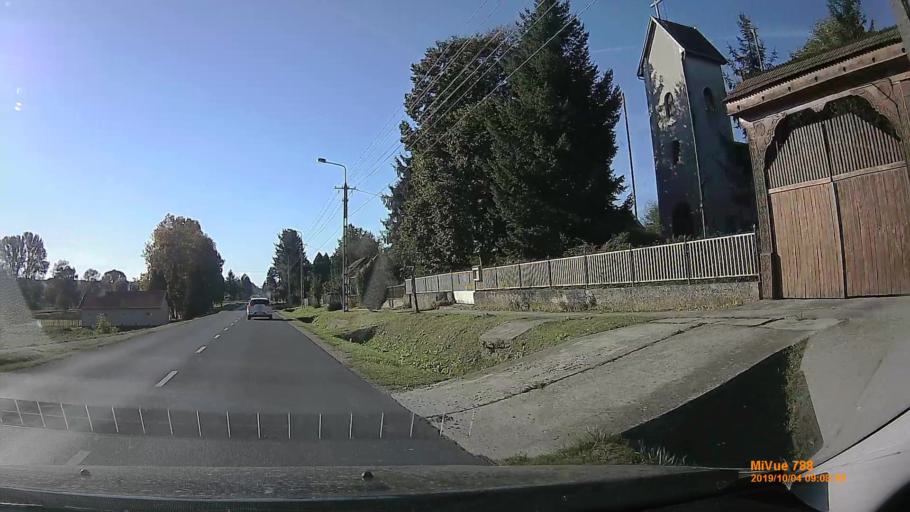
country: HU
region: Somogy
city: Karad
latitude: 46.6721
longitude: 17.7769
